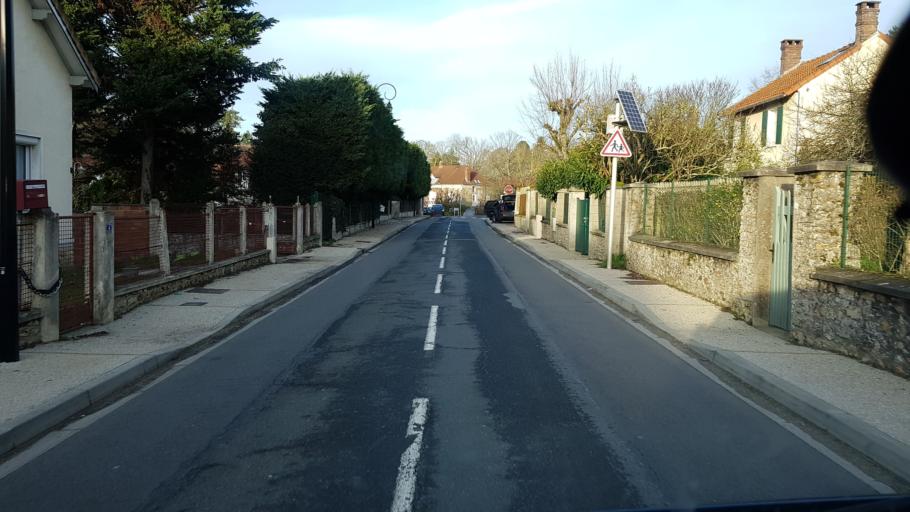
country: FR
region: Ile-de-France
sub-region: Departement des Yvelines
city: Gazeran
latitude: 48.6751
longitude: 1.7522
